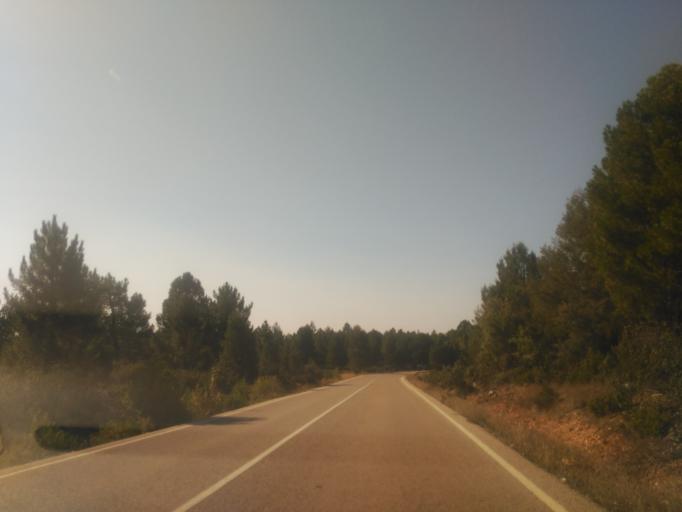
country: ES
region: Castille and Leon
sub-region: Provincia de Soria
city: Herrera de Soria
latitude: 41.7672
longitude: -3.0310
